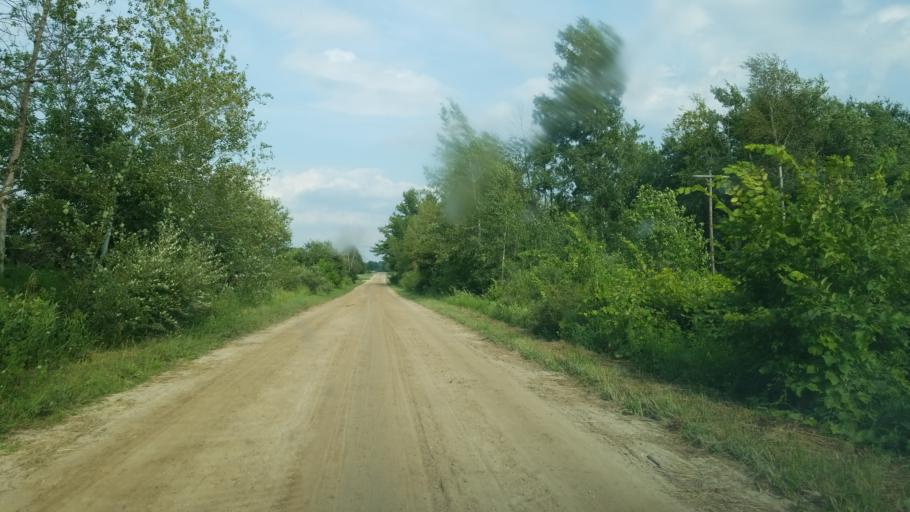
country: US
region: Michigan
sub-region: Mecosta County
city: Canadian Lakes
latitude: 43.5692
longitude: -85.3740
